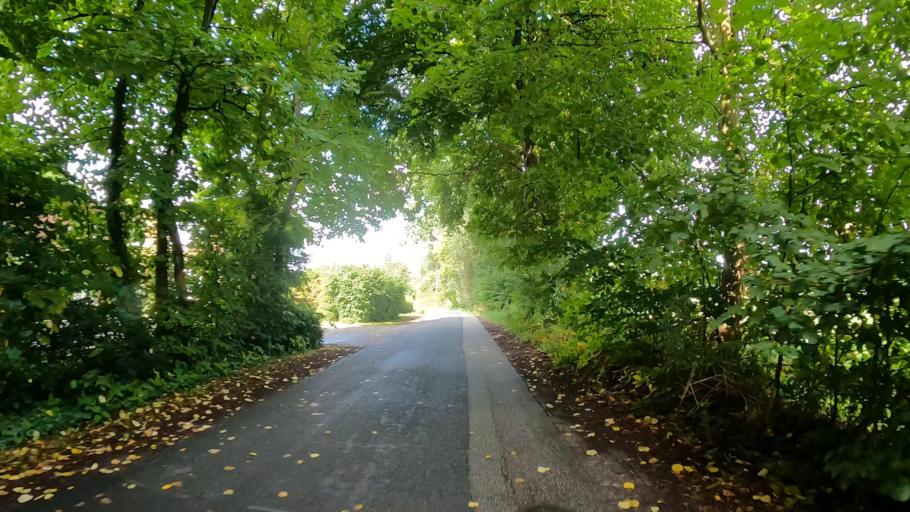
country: DE
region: Schleswig-Holstein
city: Tornesch
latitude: 53.7200
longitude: 9.7016
